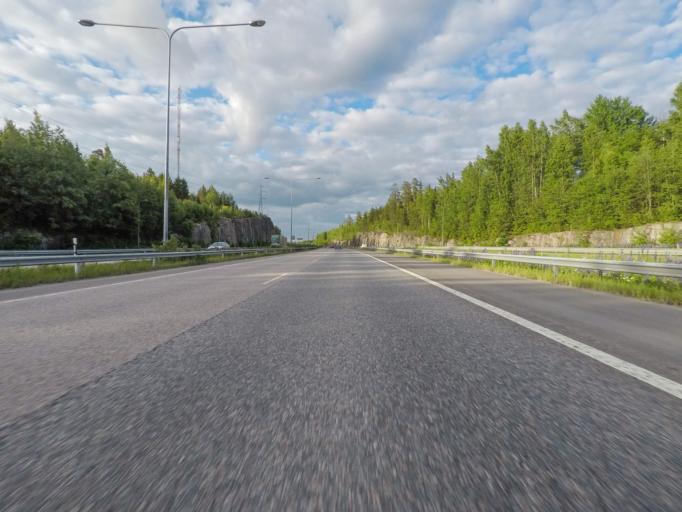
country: FI
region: Paijanne Tavastia
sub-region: Lahti
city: Lahti
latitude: 60.9723
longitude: 25.7241
